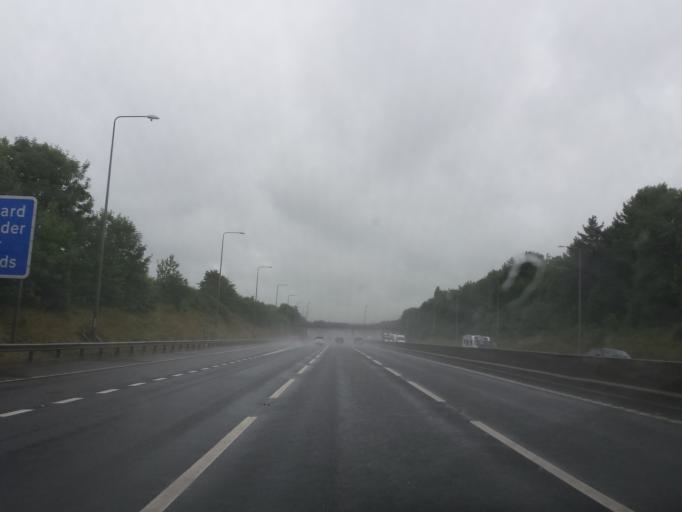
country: GB
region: England
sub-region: Derbyshire
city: Long Eaton
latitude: 52.9232
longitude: -1.3001
